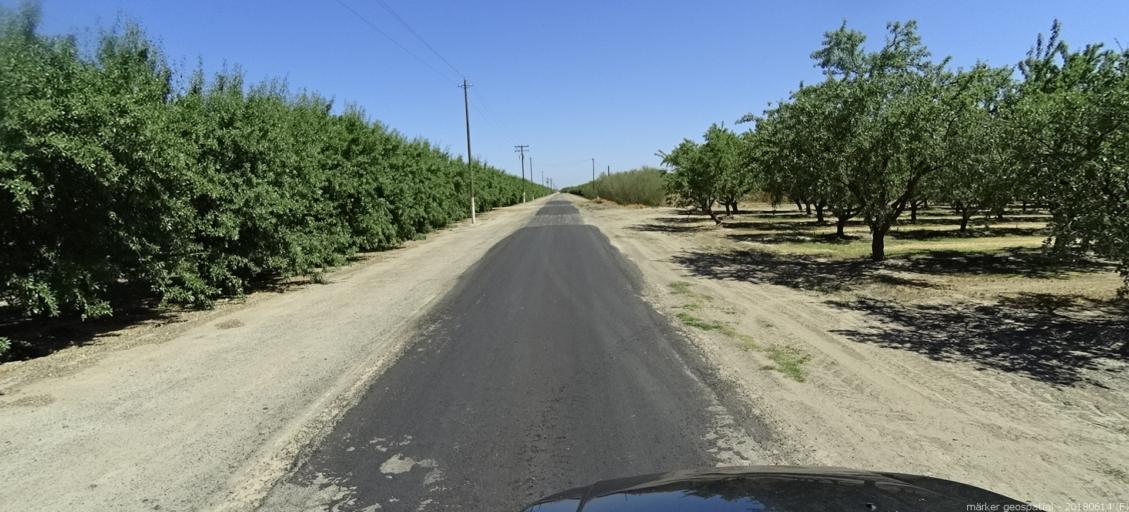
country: US
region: California
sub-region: Madera County
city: Fairmead
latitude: 36.9482
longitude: -120.2109
